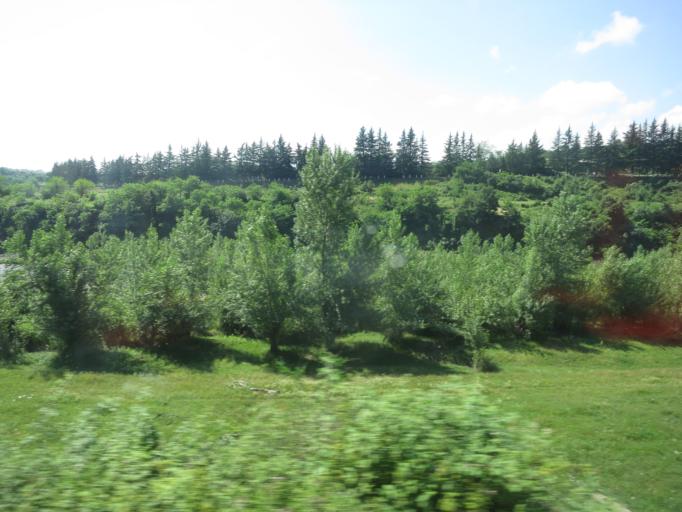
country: GE
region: Imereti
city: Zestap'oni
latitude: 42.1033
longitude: 43.0635
